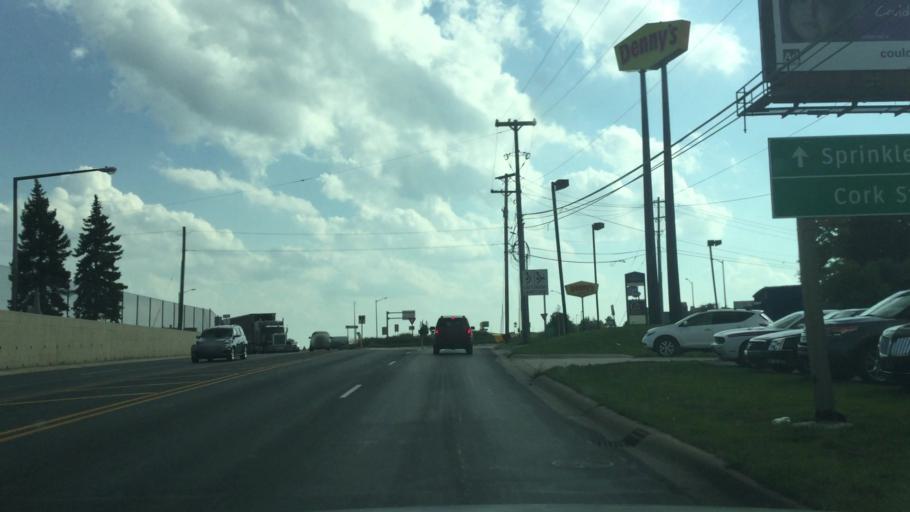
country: US
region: Michigan
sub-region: Kalamazoo County
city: Eastwood
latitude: 42.2635
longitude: -85.5309
